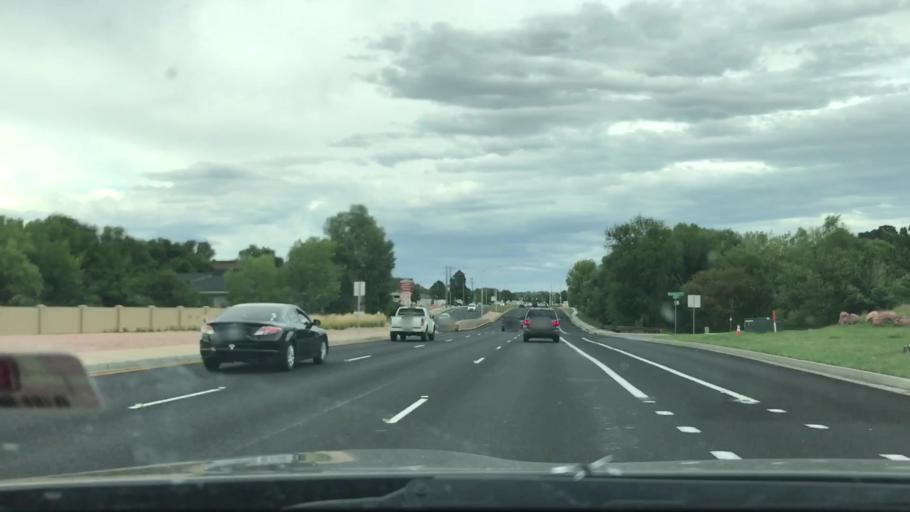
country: US
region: Colorado
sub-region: El Paso County
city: Colorado Springs
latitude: 38.8890
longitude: -104.7746
